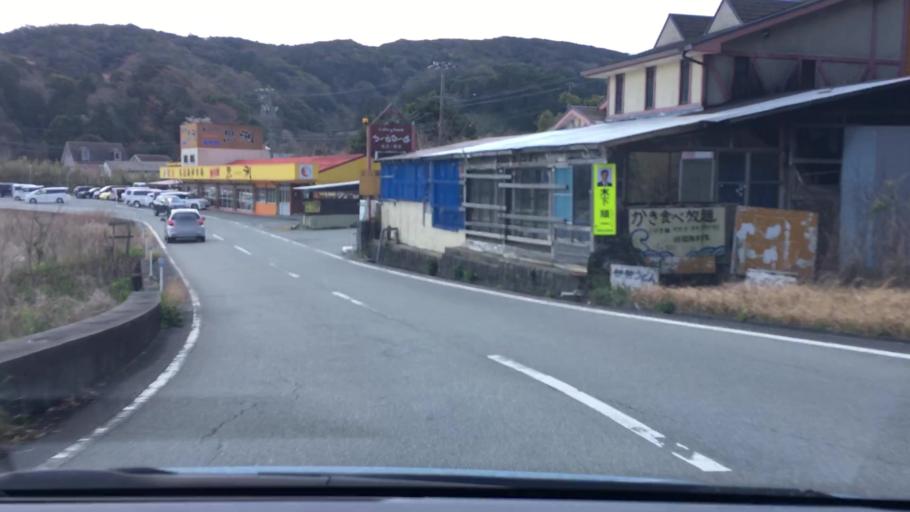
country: JP
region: Mie
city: Toba
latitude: 34.4508
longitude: 136.8746
